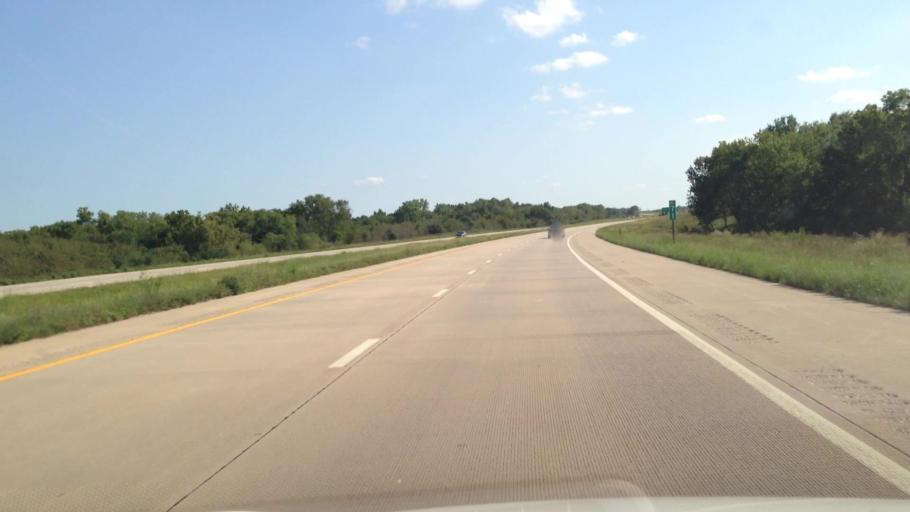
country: US
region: Kansas
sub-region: Bourbon County
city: Fort Scott
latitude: 37.9070
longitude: -94.7033
